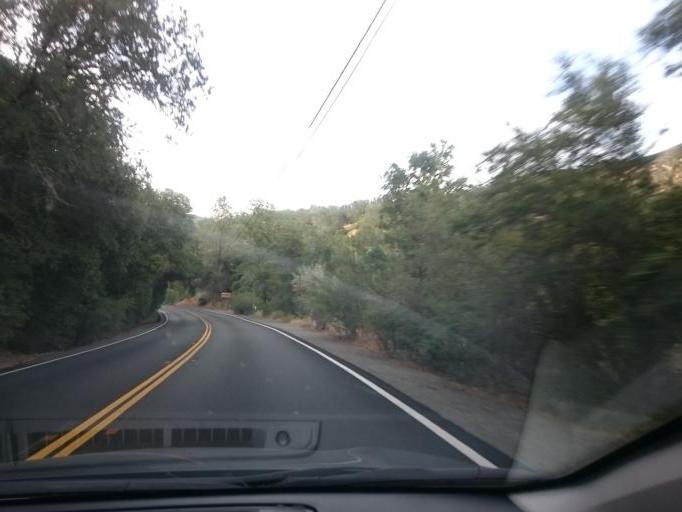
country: US
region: California
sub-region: Yolo County
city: Winters
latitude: 38.4889
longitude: -122.1271
